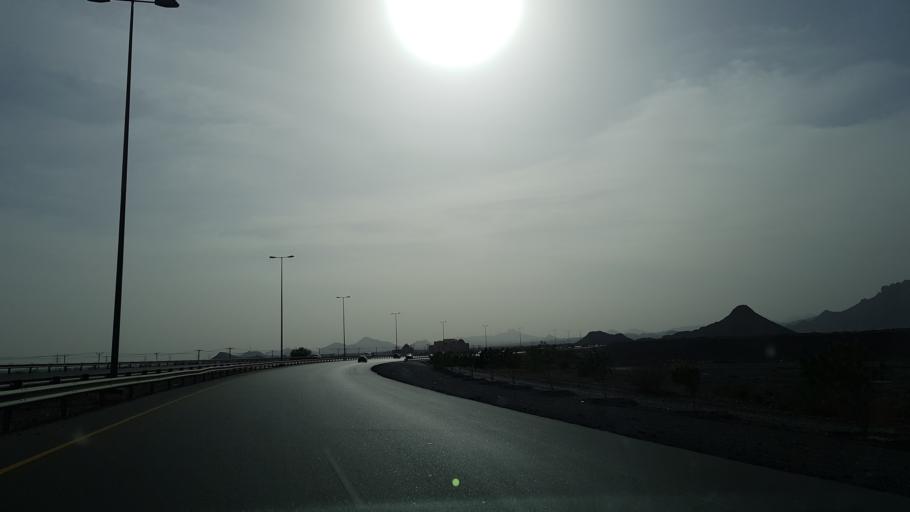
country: OM
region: Muhafazat ad Dakhiliyah
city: Nizwa
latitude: 22.8614
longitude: 57.5914
